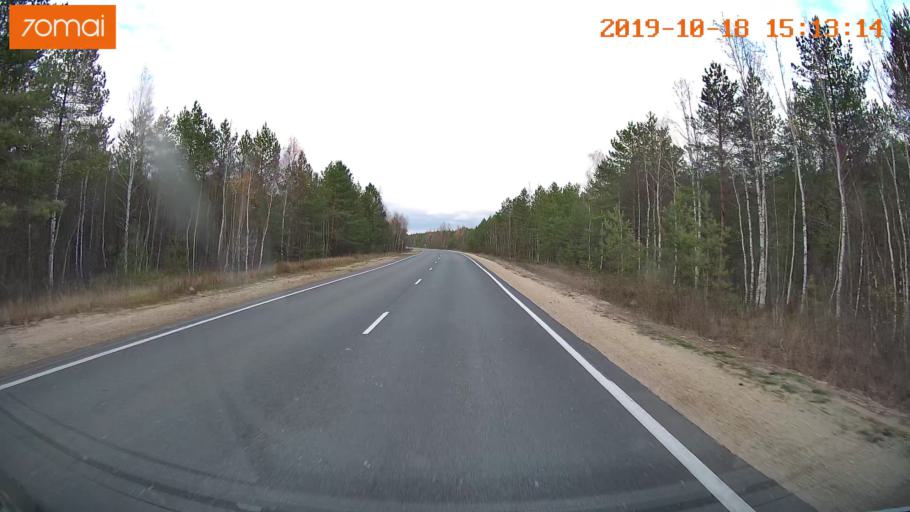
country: RU
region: Vladimir
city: Gus'-Khrustal'nyy
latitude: 55.5839
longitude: 40.7142
